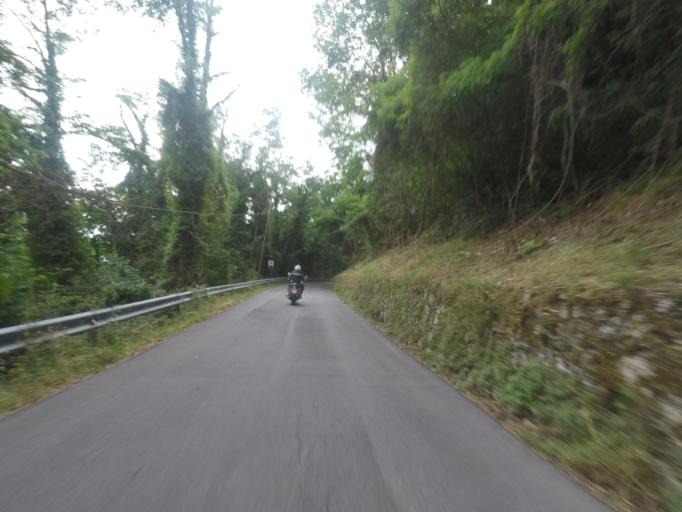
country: IT
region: Tuscany
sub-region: Provincia di Lucca
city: Castelnuovo di Garfagnana
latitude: 44.1081
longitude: 10.3728
